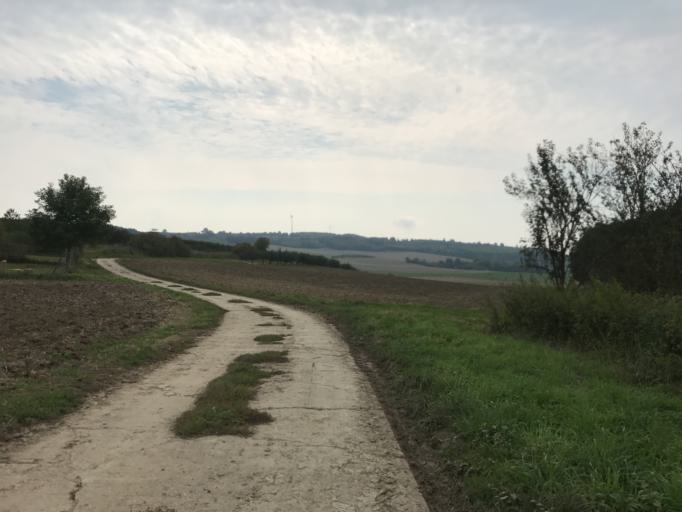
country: DE
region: Rheinland-Pfalz
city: Klein-Winternheim
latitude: 49.9302
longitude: 8.2206
